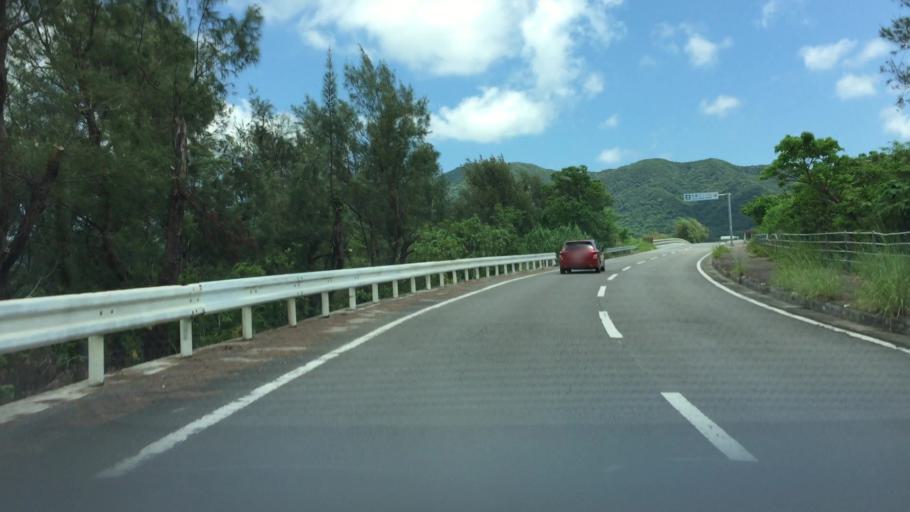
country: JP
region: Okinawa
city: Ishigaki
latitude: 24.4008
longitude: 124.1403
